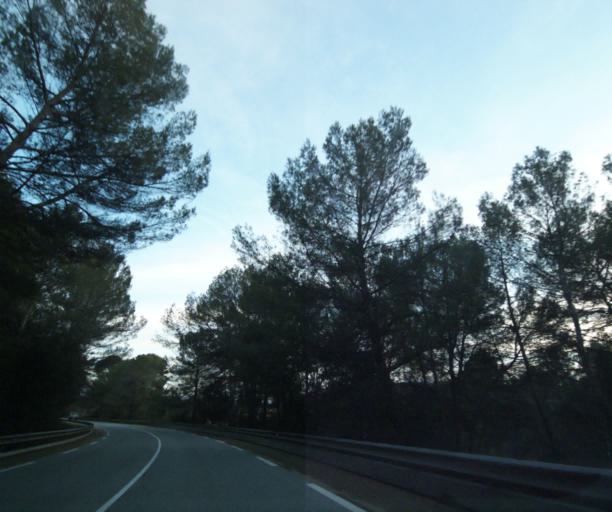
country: FR
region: Provence-Alpes-Cote d'Azur
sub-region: Departement du Var
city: La Motte
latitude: 43.4845
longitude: 6.5111
